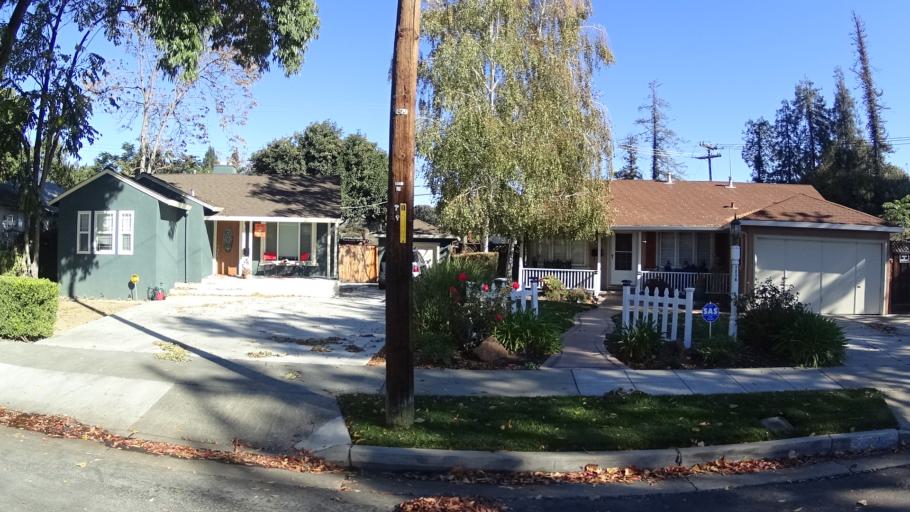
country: US
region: California
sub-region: Santa Clara County
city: San Jose
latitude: 37.3585
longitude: -121.9083
